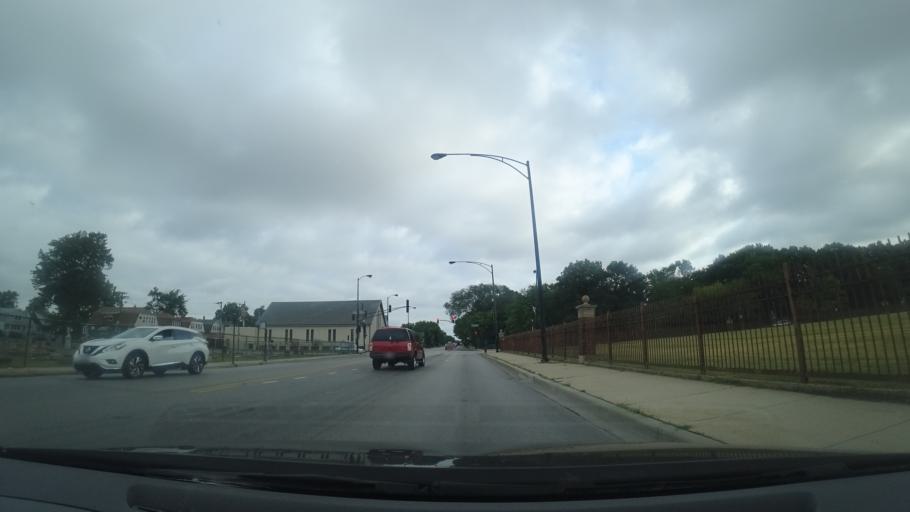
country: US
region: Illinois
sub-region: Cook County
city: Lincolnwood
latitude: 41.9823
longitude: -87.7284
